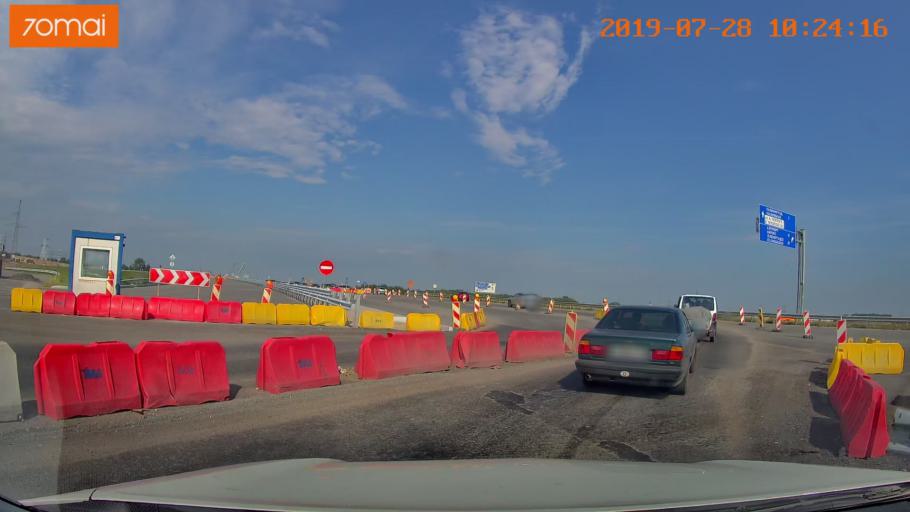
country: RU
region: Kaliningrad
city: Maloye Isakovo
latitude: 54.7681
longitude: 20.5523
